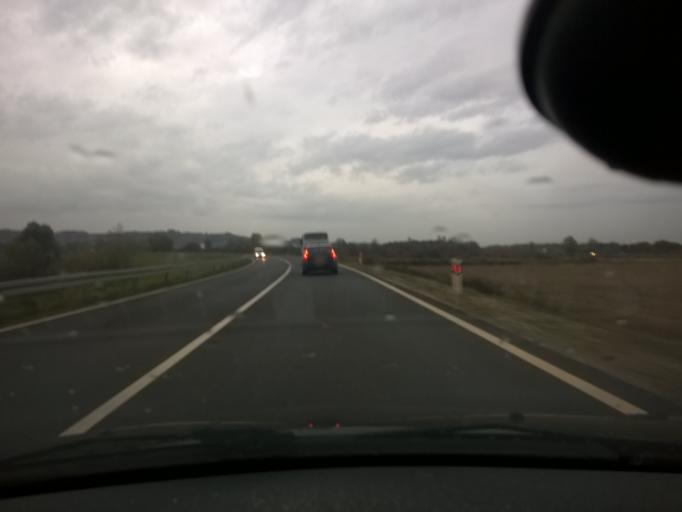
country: HR
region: Zagrebacka
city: Pojatno
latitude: 45.8926
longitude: 15.8212
